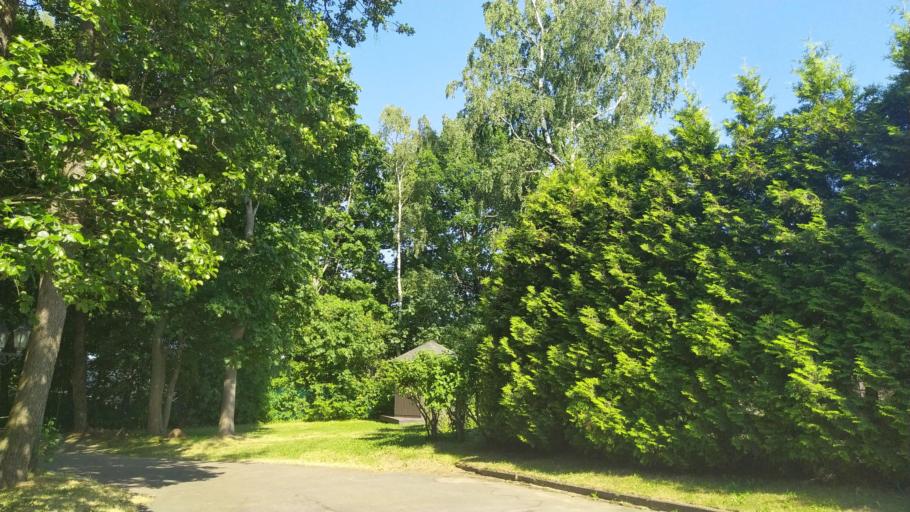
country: RU
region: St.-Petersburg
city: Repino
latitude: 60.1617
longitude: 29.8527
